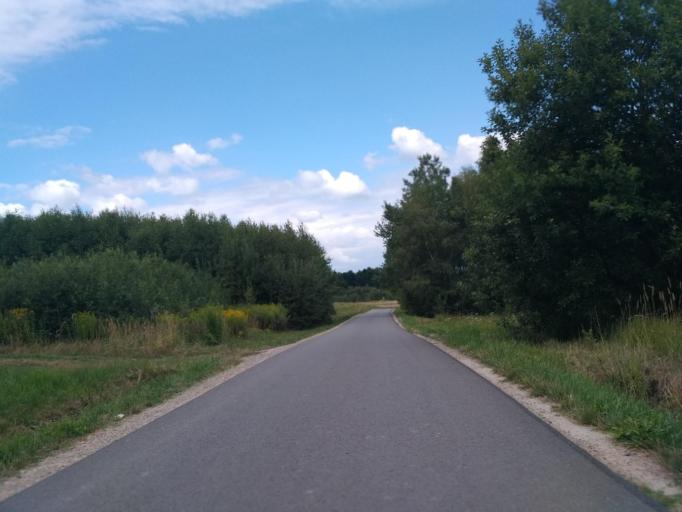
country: PL
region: Subcarpathian Voivodeship
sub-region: Powiat rzeszowski
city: Hyzne
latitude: 49.9035
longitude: 22.2259
